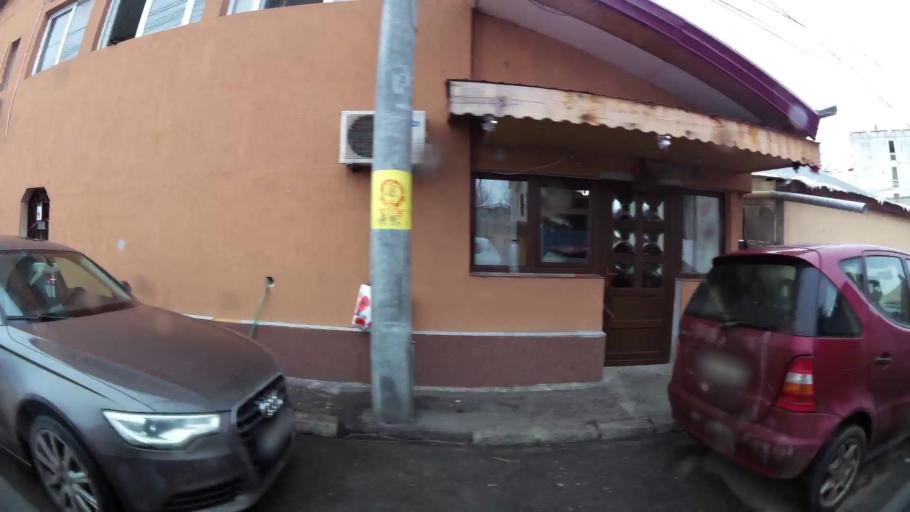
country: RO
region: Ilfov
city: Dobroesti
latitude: 44.4228
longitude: 26.1819
